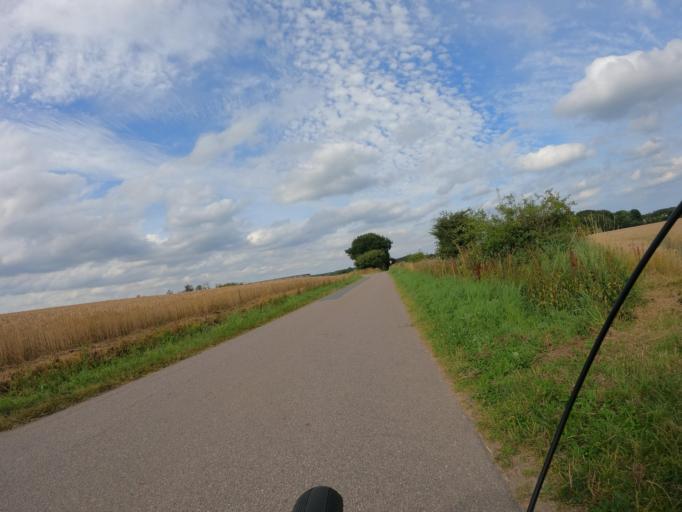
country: DE
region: Schleswig-Holstein
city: Steinberg
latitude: 54.7674
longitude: 9.7765
